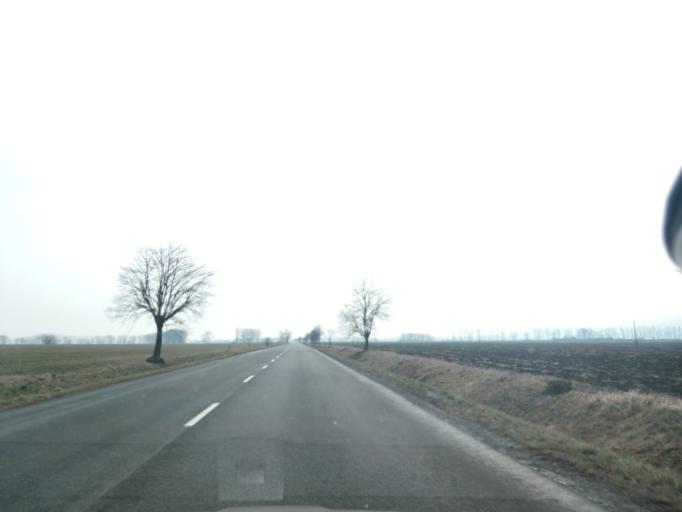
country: SK
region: Kosicky
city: Trebisov
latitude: 48.5544
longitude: 21.6785
